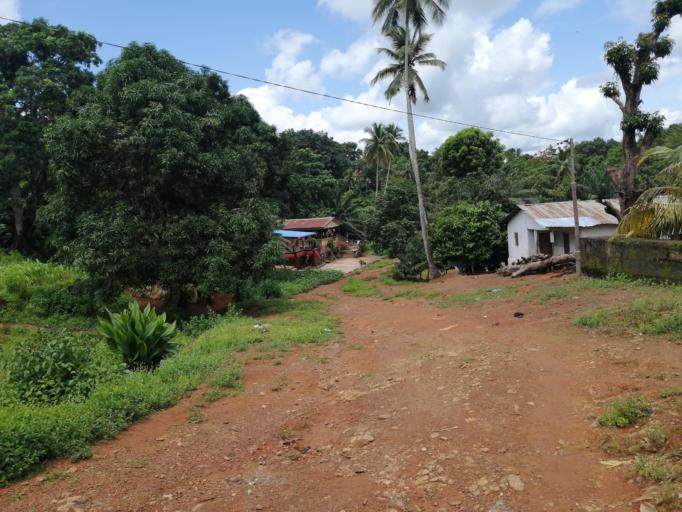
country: SL
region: Northern Province
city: Port Loko
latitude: 8.7654
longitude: -12.7928
